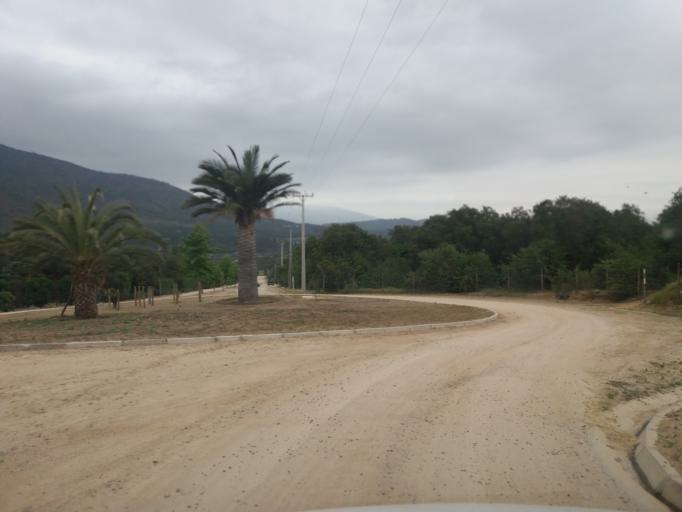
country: CL
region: Valparaiso
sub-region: Provincia de Marga Marga
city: Limache
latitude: -33.0260
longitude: -71.1317
